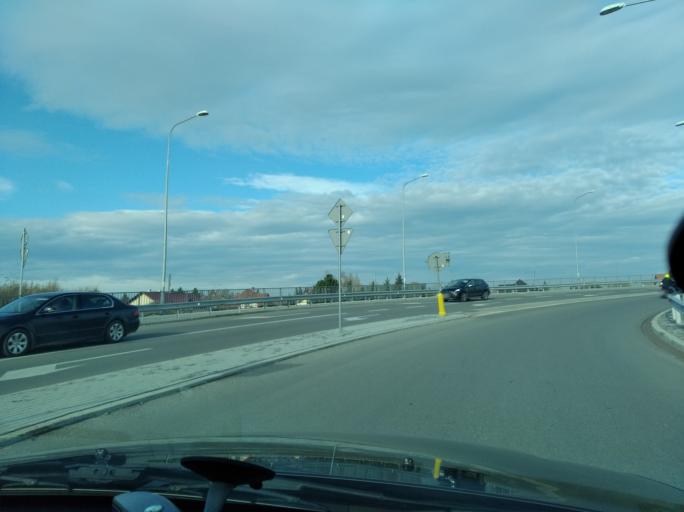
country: PL
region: Subcarpathian Voivodeship
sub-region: Powiat ropczycko-sedziszowski
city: Sedziszow Malopolski
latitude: 50.0760
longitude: 21.6924
